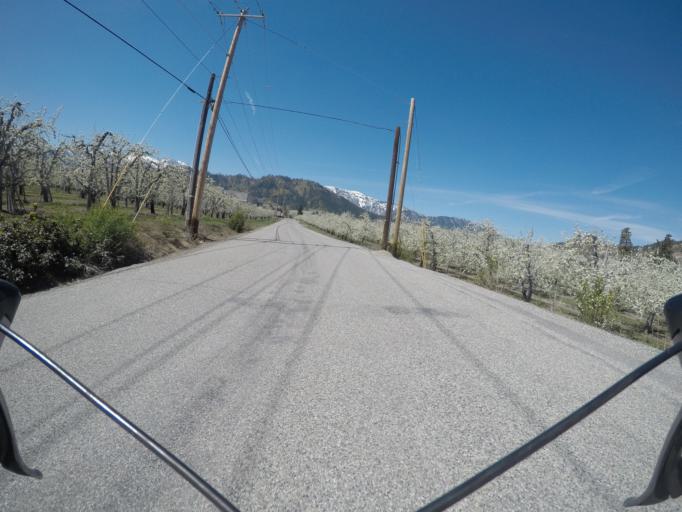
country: US
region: Washington
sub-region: Chelan County
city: Leavenworth
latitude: 47.5642
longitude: -120.5830
